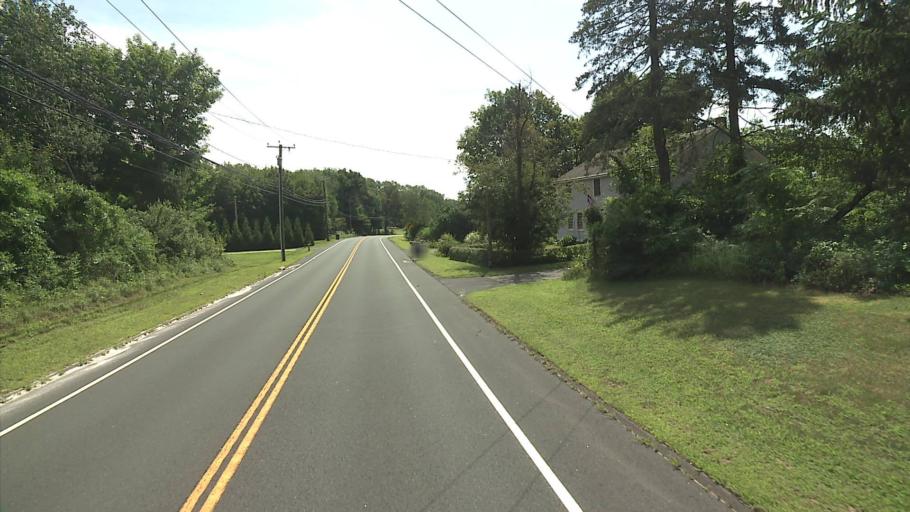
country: US
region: Connecticut
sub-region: Tolland County
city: Rockville
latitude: 41.8393
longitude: -72.4110
